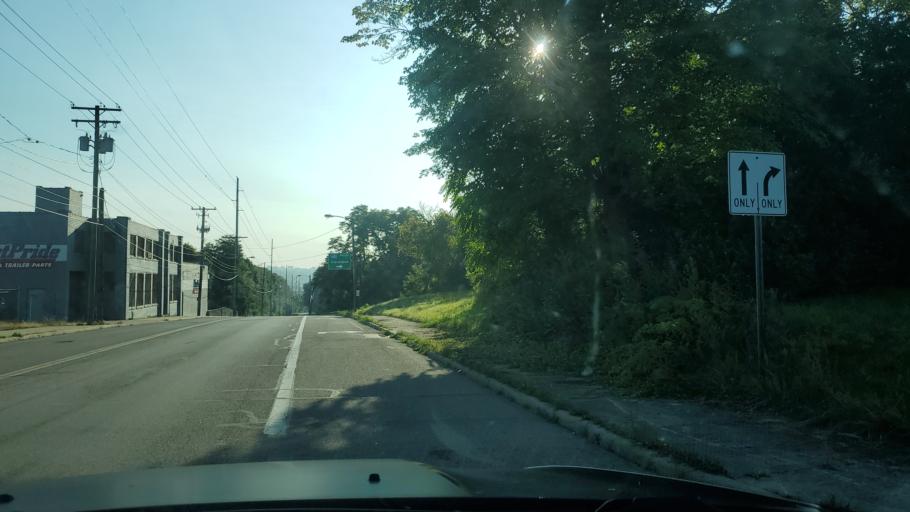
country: US
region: Ohio
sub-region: Mahoning County
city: Youngstown
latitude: 41.0932
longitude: -80.6529
